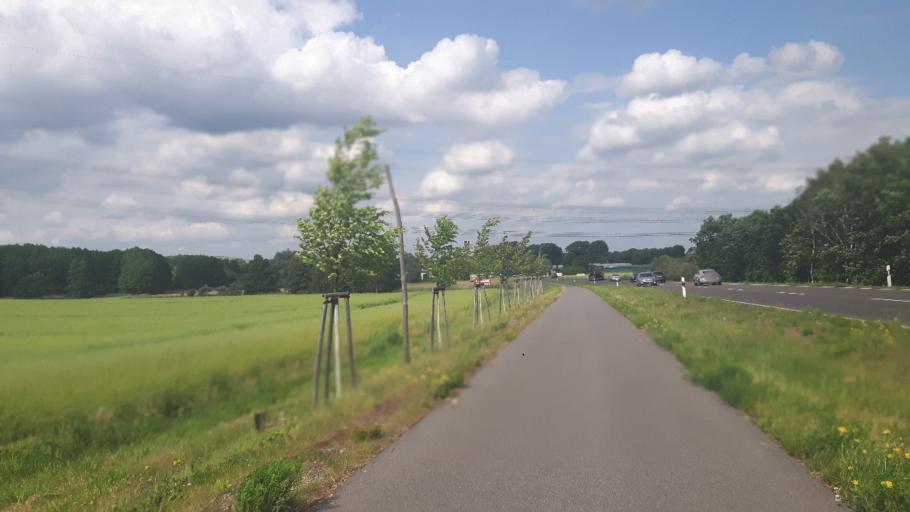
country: DE
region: Berlin
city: Buch
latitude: 52.6175
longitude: 13.5399
